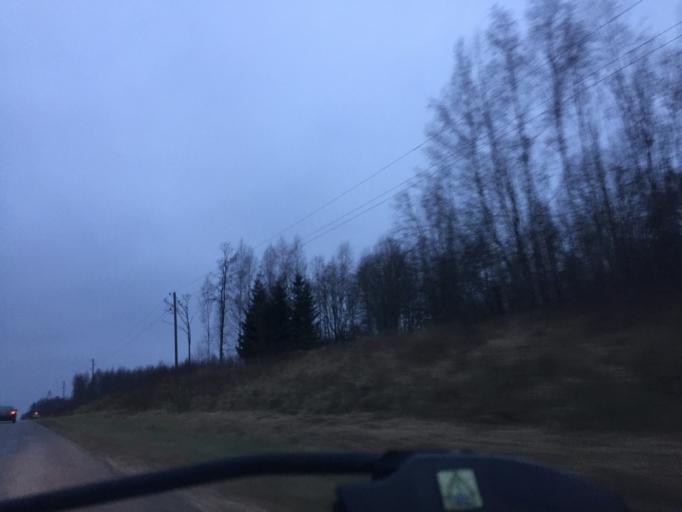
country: LV
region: Limbazu Rajons
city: Limbazi
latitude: 57.6044
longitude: 24.8087
